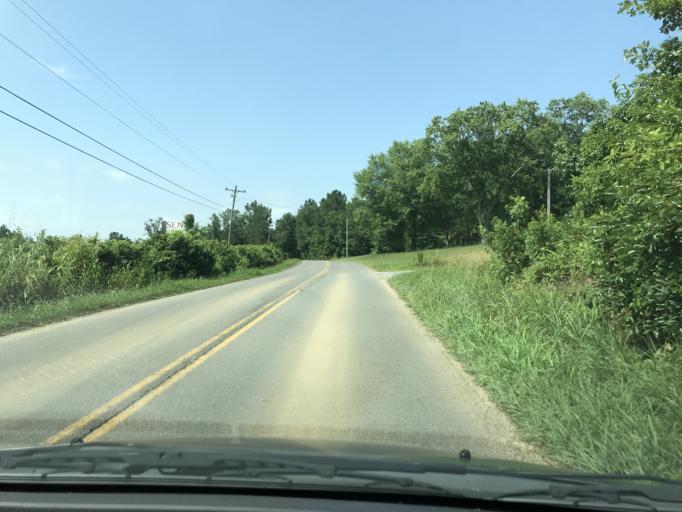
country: US
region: Tennessee
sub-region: Hamilton County
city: Apison
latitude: 35.0513
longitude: -84.9873
